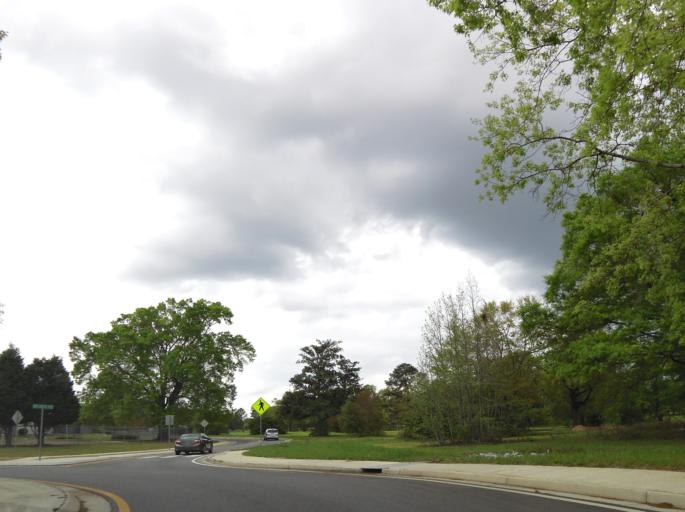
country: US
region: Georgia
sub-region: Houston County
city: Warner Robins
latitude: 32.6135
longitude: -83.6034
